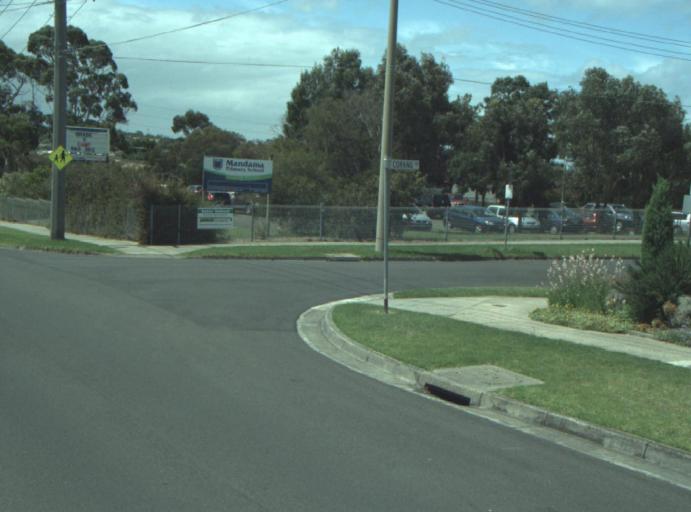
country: AU
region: Victoria
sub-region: Greater Geelong
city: Wandana Heights
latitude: -38.2005
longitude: 144.3269
